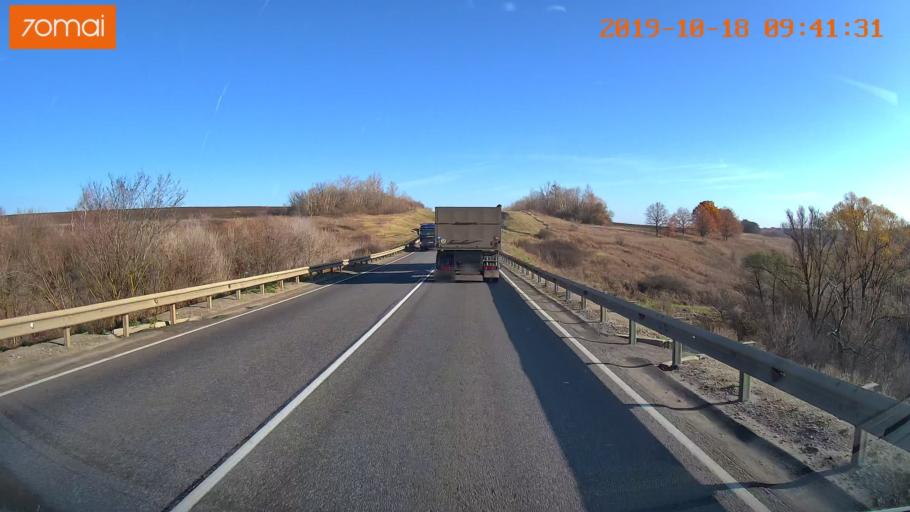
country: RU
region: Tula
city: Kazachka
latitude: 53.2758
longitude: 38.1630
